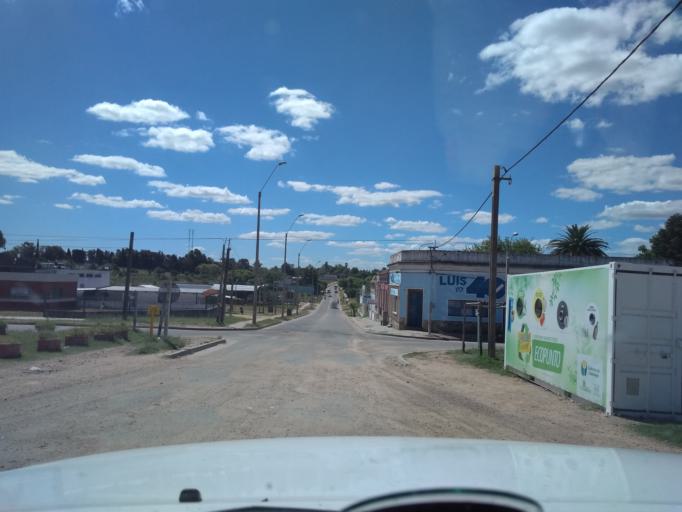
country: UY
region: Canelones
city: Pando
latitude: -34.7157
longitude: -55.9623
